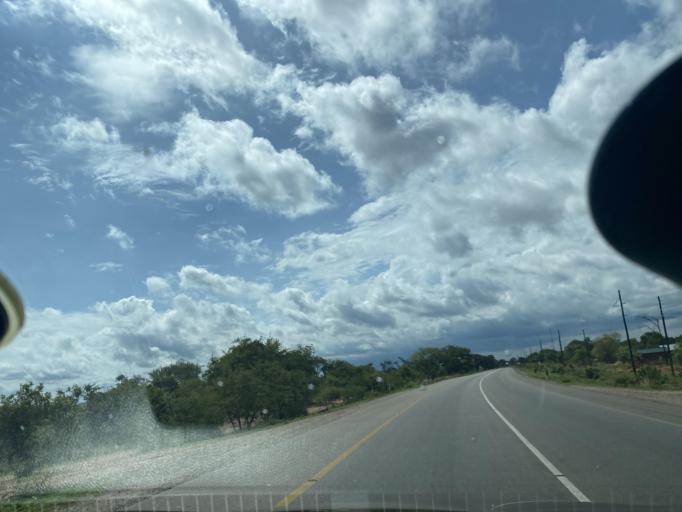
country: ZM
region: Lusaka
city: Kafue
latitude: -15.8573
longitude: 28.2598
